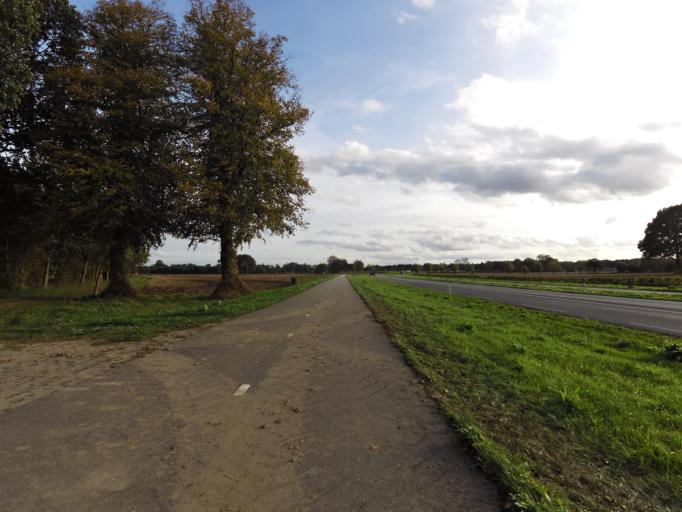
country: NL
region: Gelderland
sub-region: Gemeente Bronckhorst
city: Baak
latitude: 52.0121
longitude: 6.2288
